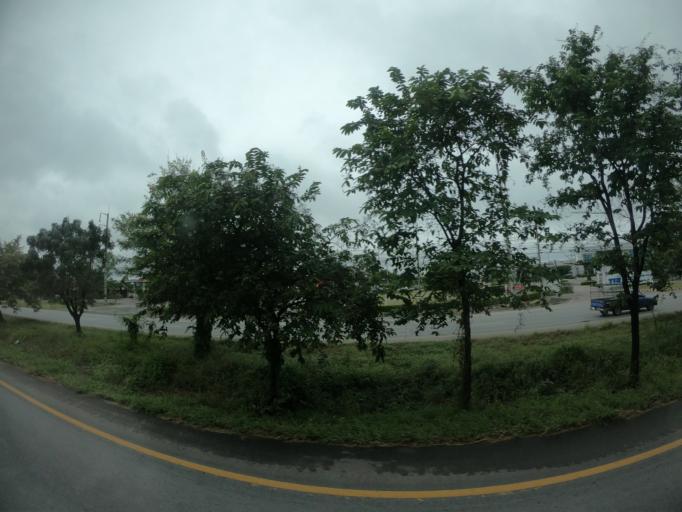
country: TH
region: Nakhon Ratchasima
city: Chaloem Phra Kiat
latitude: 15.0678
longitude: 102.1989
